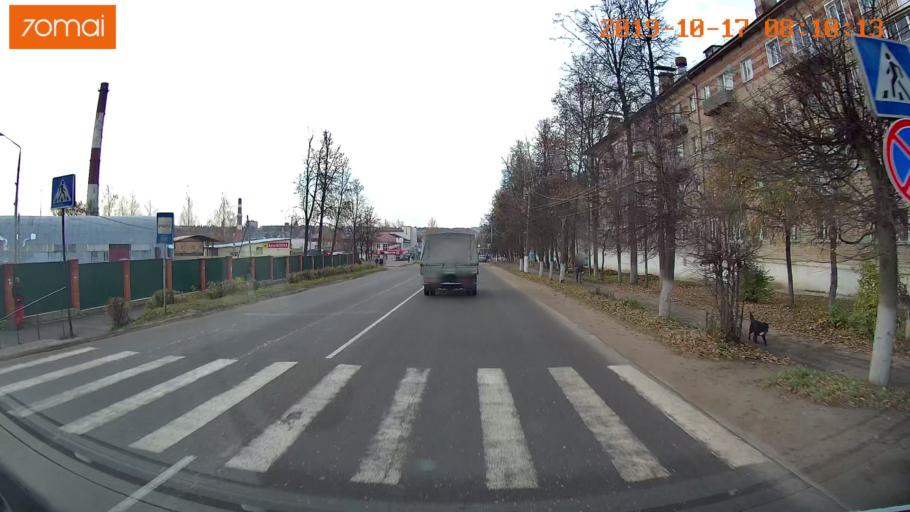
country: RU
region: Vladimir
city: Kol'chugino
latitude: 56.3088
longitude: 39.3782
